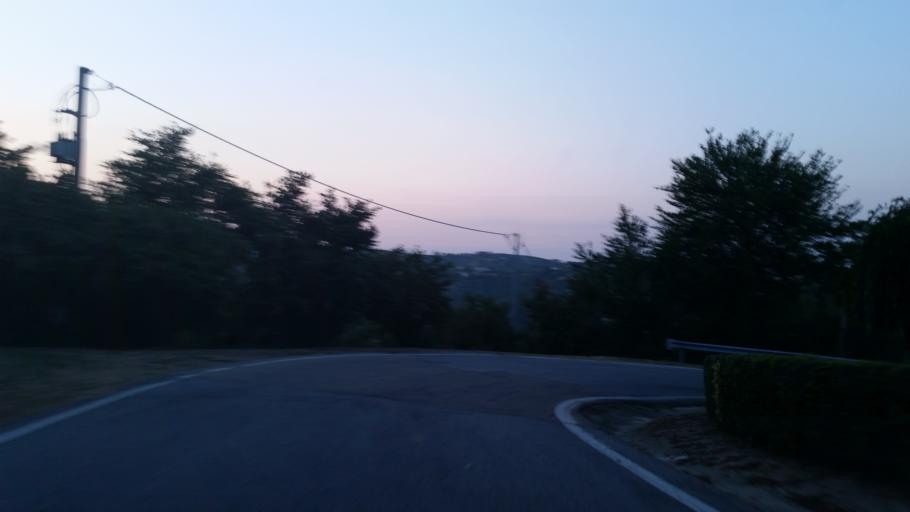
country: IT
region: Piedmont
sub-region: Provincia di Cuneo
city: Camo
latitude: 44.6950
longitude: 8.1954
